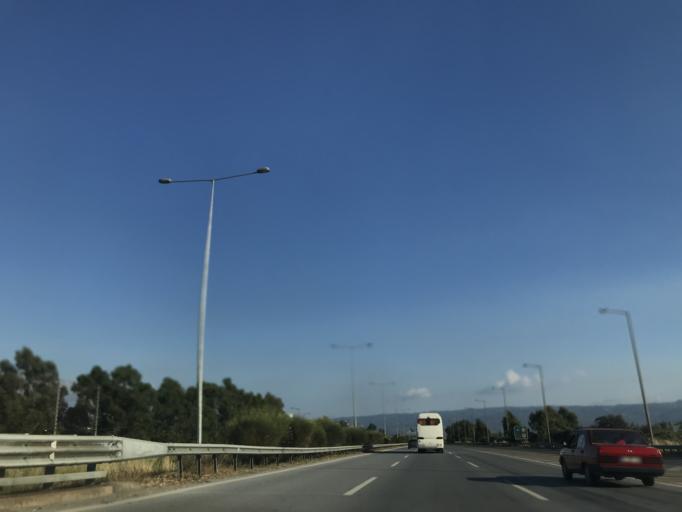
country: TR
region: Aydin
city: Aydin
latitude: 37.8439
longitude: 27.8083
